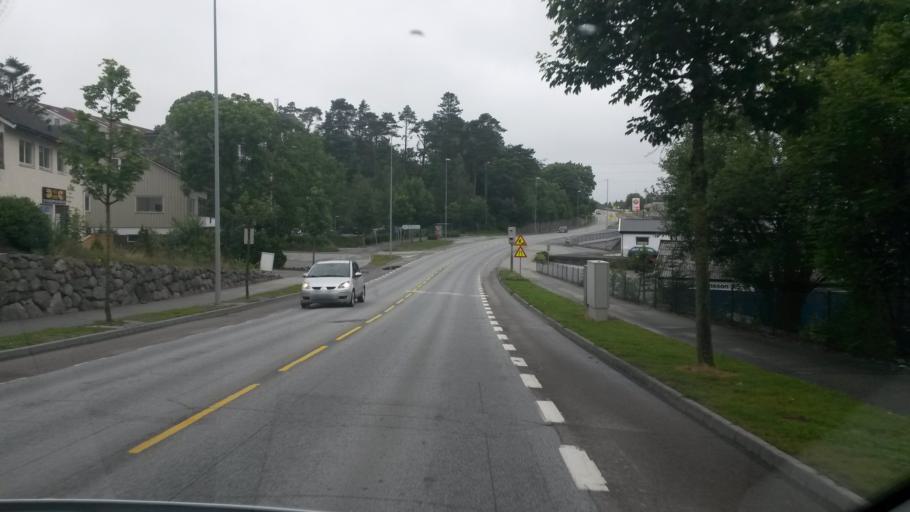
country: NO
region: Rogaland
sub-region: Sandnes
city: Sandnes
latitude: 58.8327
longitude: 5.7187
